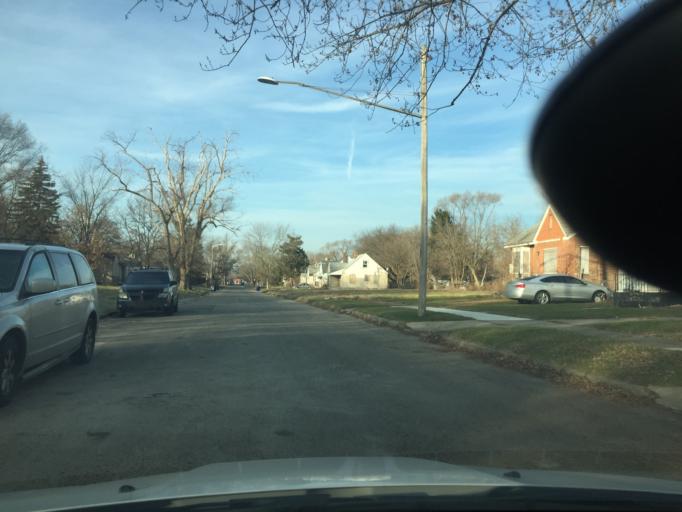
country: US
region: Michigan
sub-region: Macomb County
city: Eastpointe
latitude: 42.4410
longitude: -82.9664
